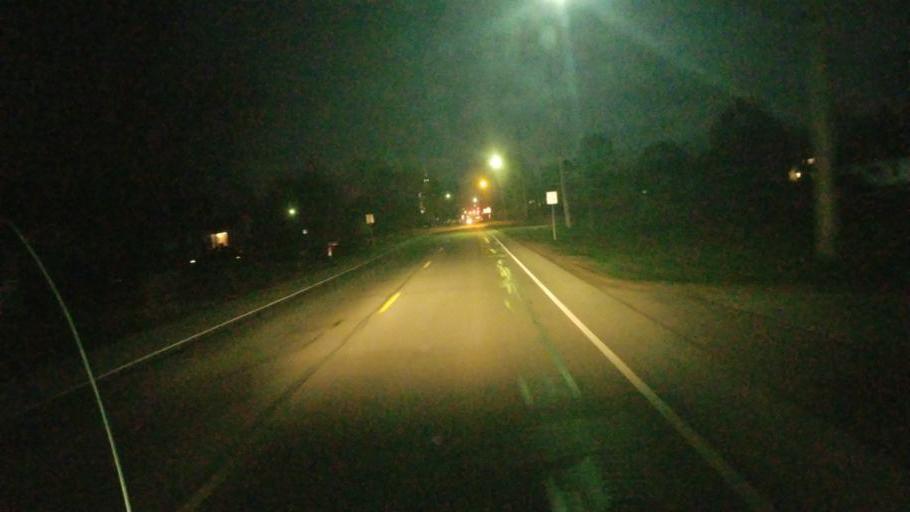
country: US
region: Indiana
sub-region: Adams County
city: Berne
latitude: 40.6574
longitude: -84.9620
